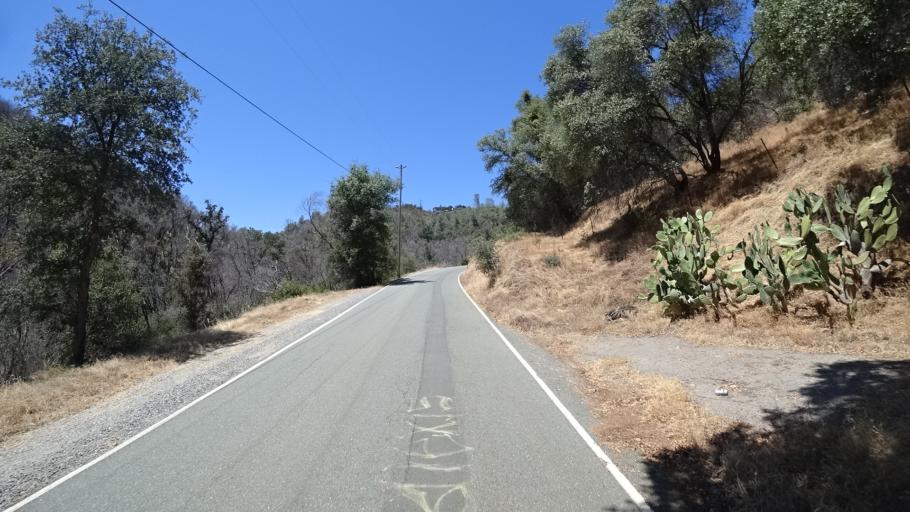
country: US
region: California
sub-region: Calaveras County
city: San Andreas
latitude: 38.2950
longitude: -120.6750
